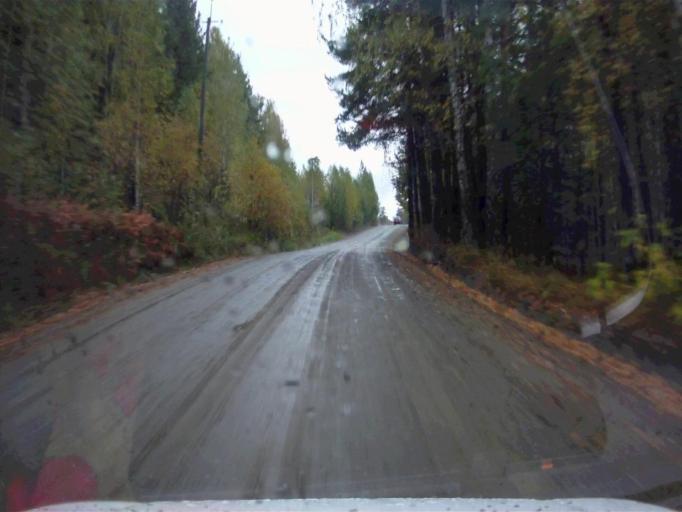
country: RU
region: Chelyabinsk
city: Kyshtym
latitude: 55.7523
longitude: 60.4868
